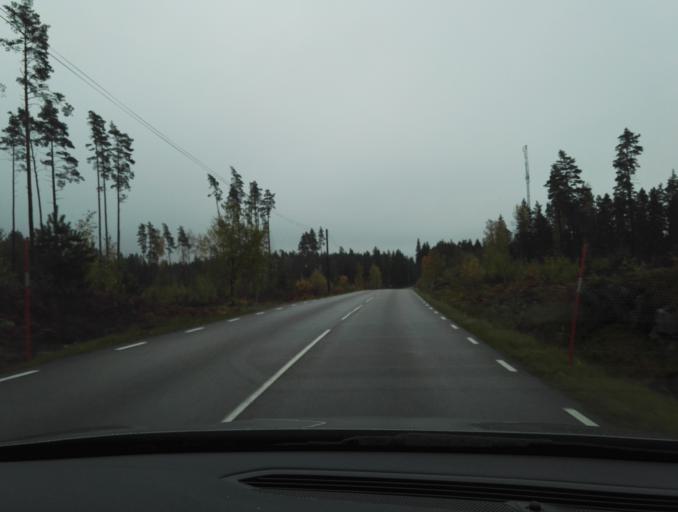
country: SE
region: Kronoberg
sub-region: Vaxjo Kommun
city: Rottne
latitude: 57.0264
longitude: 14.8286
